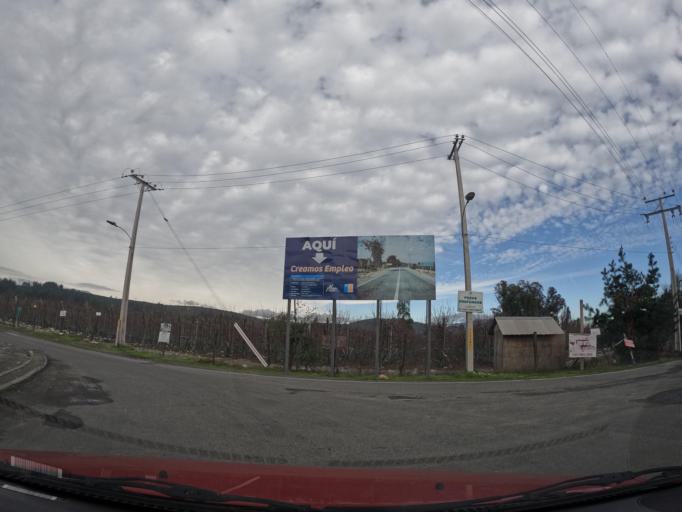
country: CL
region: Maule
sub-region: Provincia de Linares
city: Linares
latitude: -35.9126
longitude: -71.4932
